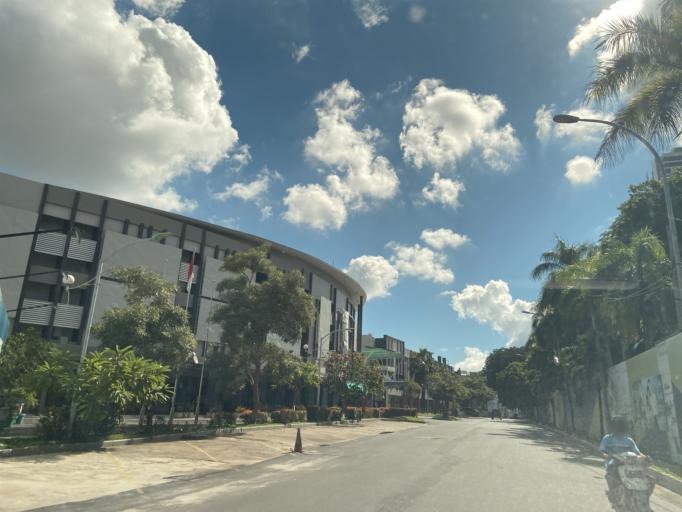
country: SG
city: Singapore
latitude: 1.1431
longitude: 104.0073
